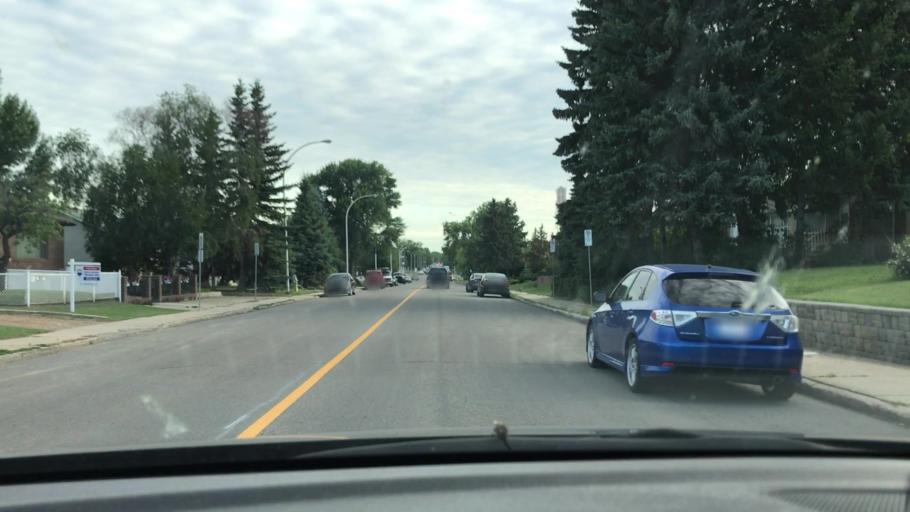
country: CA
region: Alberta
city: Edmonton
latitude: 53.5388
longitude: -113.4493
